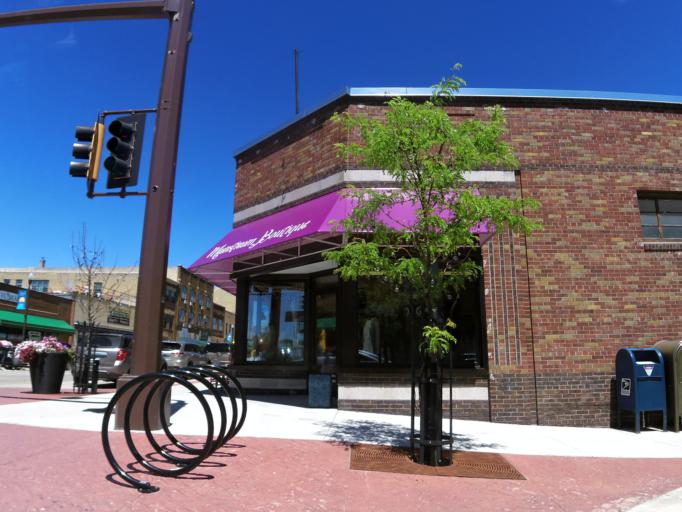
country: US
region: Minnesota
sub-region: Becker County
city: Detroit Lakes
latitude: 46.8172
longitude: -95.8451
